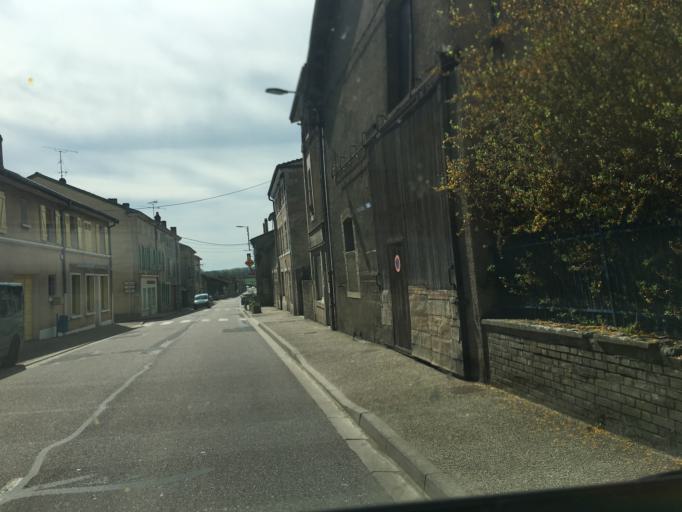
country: FR
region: Lorraine
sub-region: Departement de la Meuse
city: Lerouville
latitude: 48.8254
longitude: 5.5102
